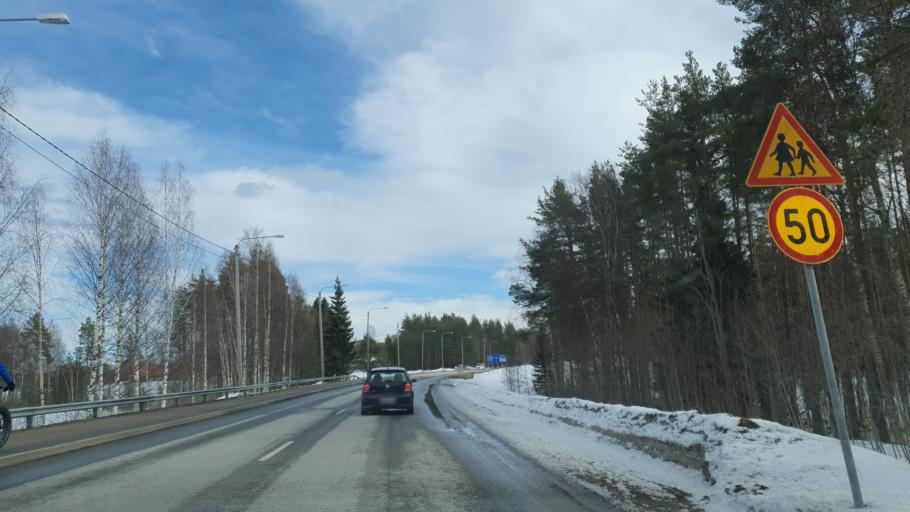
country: FI
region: Kainuu
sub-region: Kajaani
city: Vuokatti
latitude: 64.1474
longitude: 28.3000
